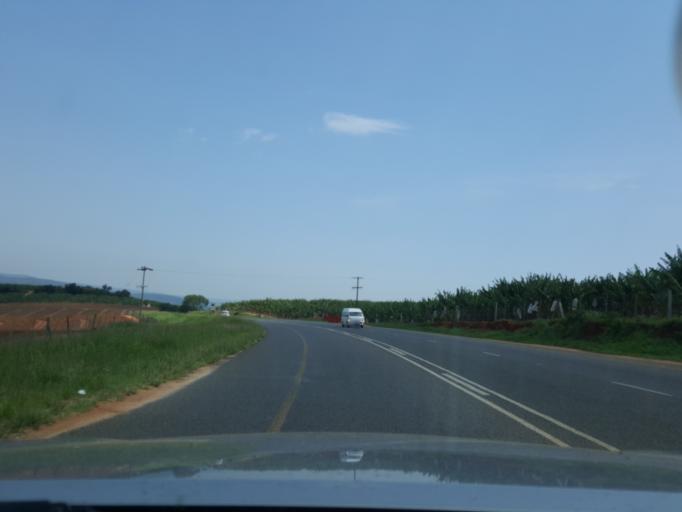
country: ZA
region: Mpumalanga
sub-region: Ehlanzeni District
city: White River
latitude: -25.0773
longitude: 31.1040
